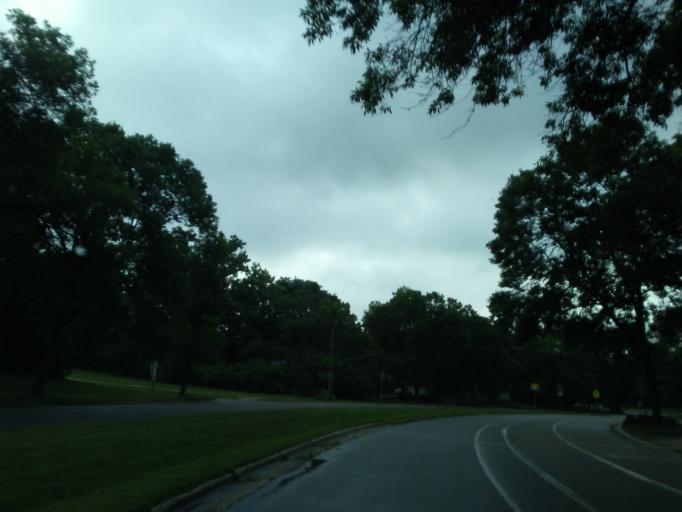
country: US
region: Wisconsin
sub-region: Dane County
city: Shorewood Hills
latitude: 43.0636
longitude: -89.4576
